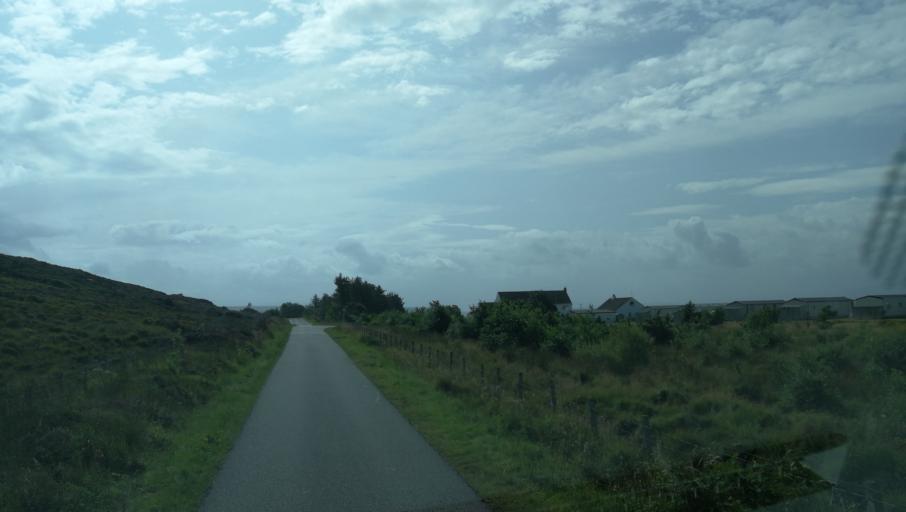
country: GB
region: Scotland
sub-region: Highland
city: Portree
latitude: 57.7422
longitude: -5.7637
